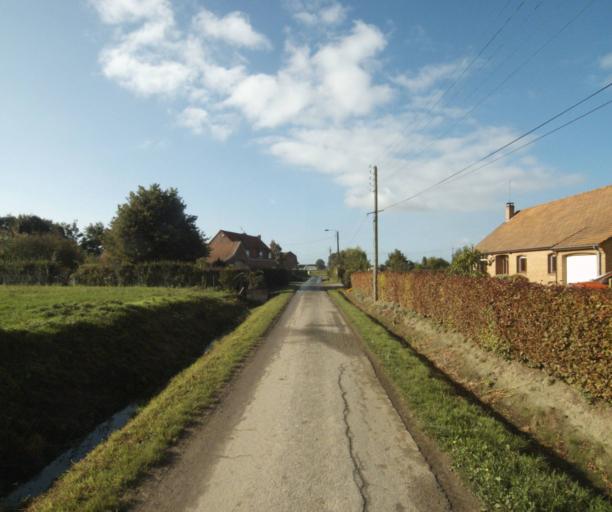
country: FR
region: Nord-Pas-de-Calais
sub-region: Departement du Nord
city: Verlinghem
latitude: 50.6864
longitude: 2.9805
